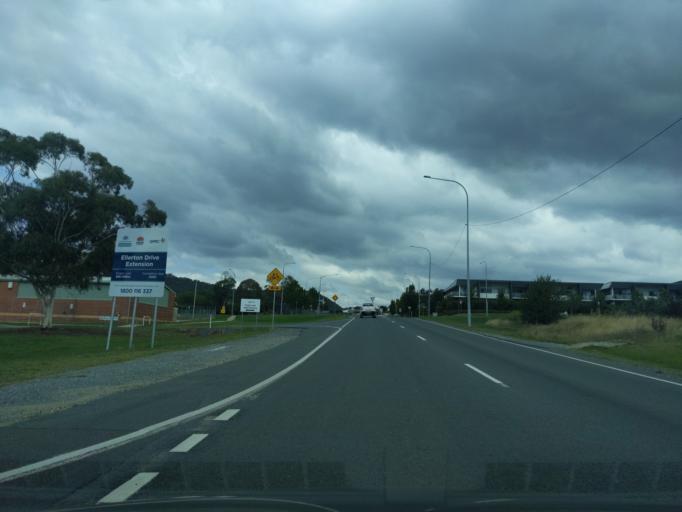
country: AU
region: New South Wales
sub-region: Queanbeyan
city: Queanbeyan
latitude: -35.3498
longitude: 149.2462
